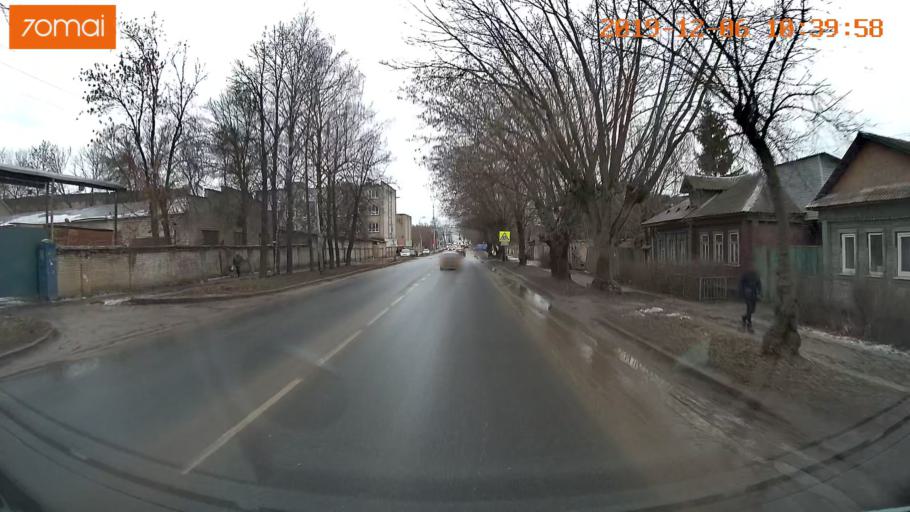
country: RU
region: Ivanovo
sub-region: Gorod Ivanovo
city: Ivanovo
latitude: 57.0300
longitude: 40.9750
